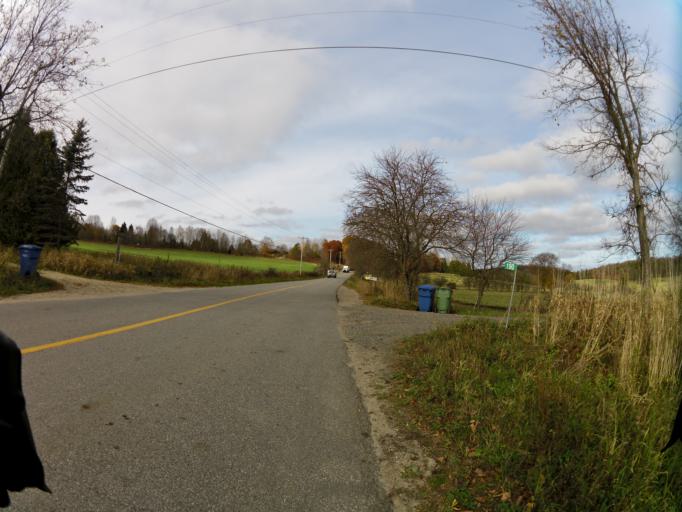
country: CA
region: Quebec
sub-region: Outaouais
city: Wakefield
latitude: 45.7221
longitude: -75.9693
